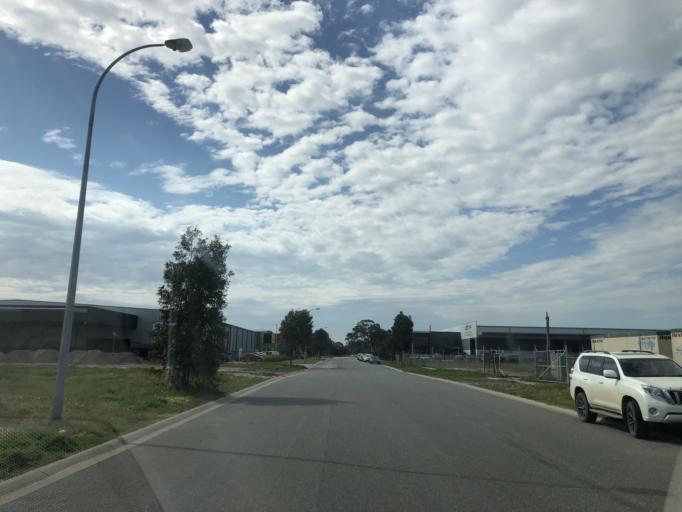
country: AU
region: Victoria
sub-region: Casey
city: Hampton Park
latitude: -38.0427
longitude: 145.2141
